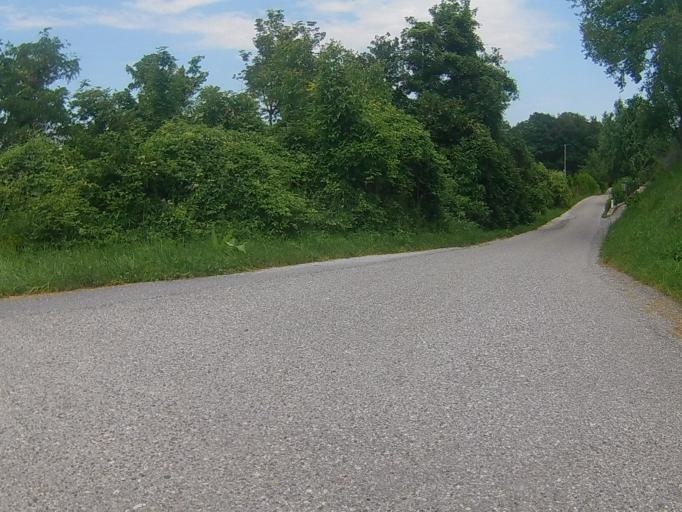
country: SI
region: Maribor
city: Kamnica
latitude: 46.5983
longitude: 15.6307
